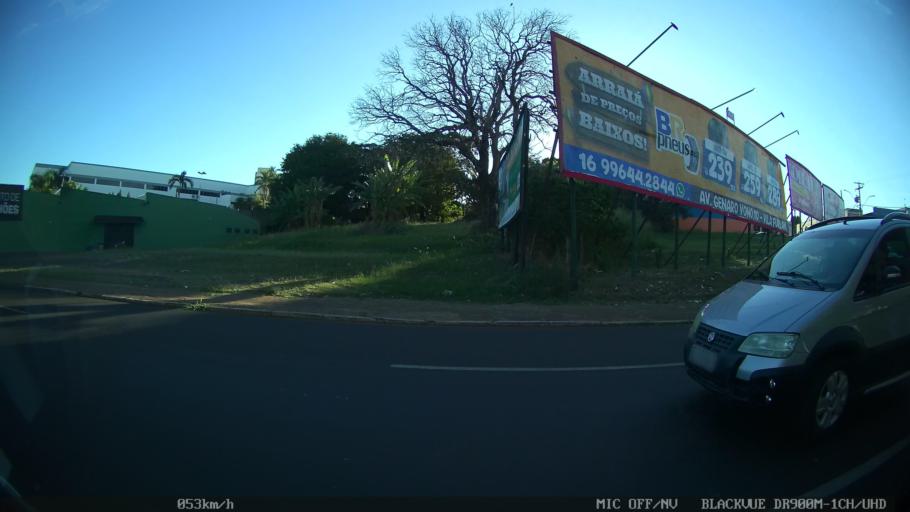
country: BR
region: Sao Paulo
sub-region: Araraquara
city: Araraquara
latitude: -21.7828
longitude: -48.1717
